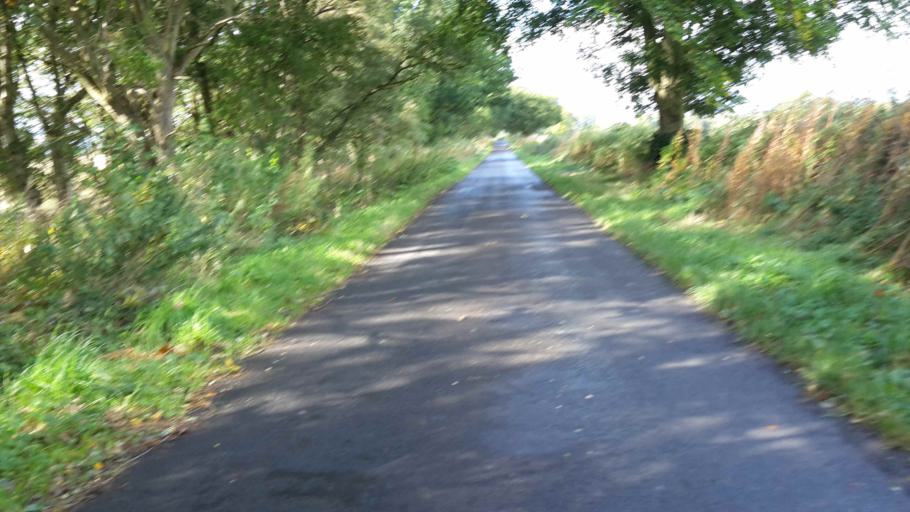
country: GB
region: Scotland
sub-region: South Lanarkshire
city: Carluke
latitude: 55.7249
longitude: -3.8597
